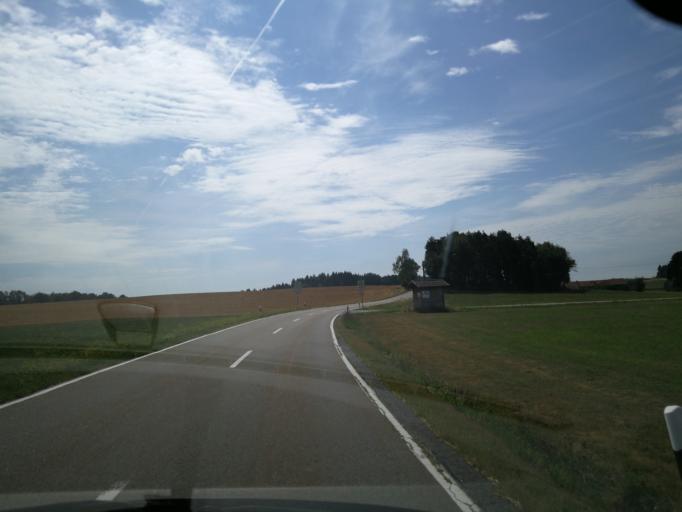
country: DE
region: Bavaria
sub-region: Lower Bavaria
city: Falkenfels
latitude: 49.0546
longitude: 12.5847
